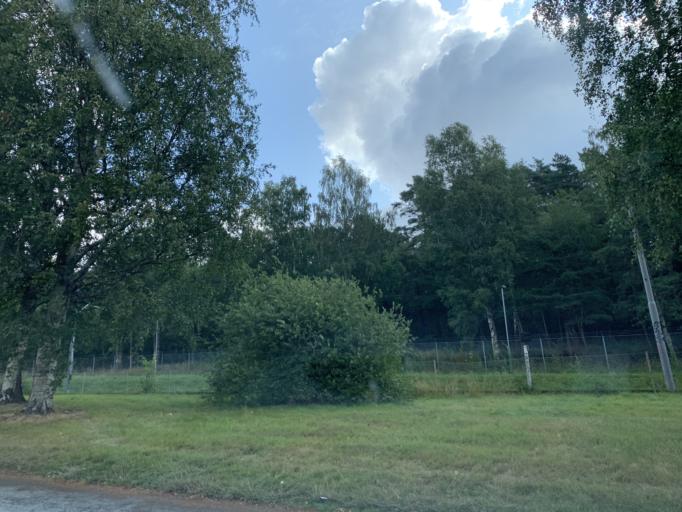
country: SE
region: Vaestra Goetaland
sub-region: Goteborg
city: Eriksbo
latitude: 57.7409
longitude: 12.0291
